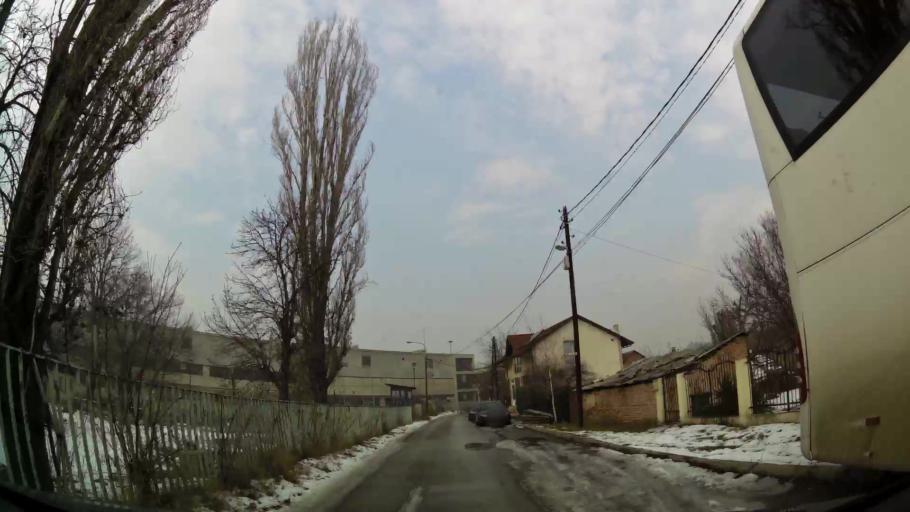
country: MK
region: Cair
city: Cair
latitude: 41.9955
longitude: 21.4582
